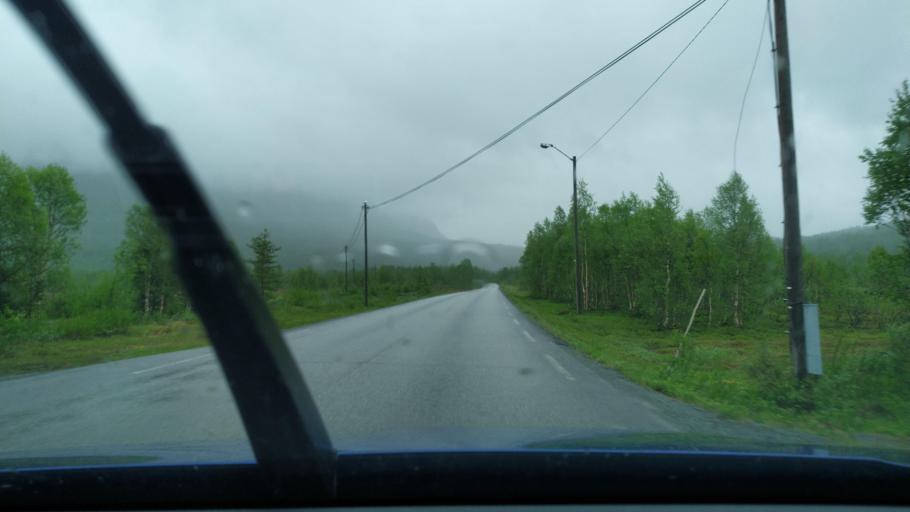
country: NO
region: Troms
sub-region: Dyroy
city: Brostadbotn
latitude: 69.0314
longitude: 17.7386
